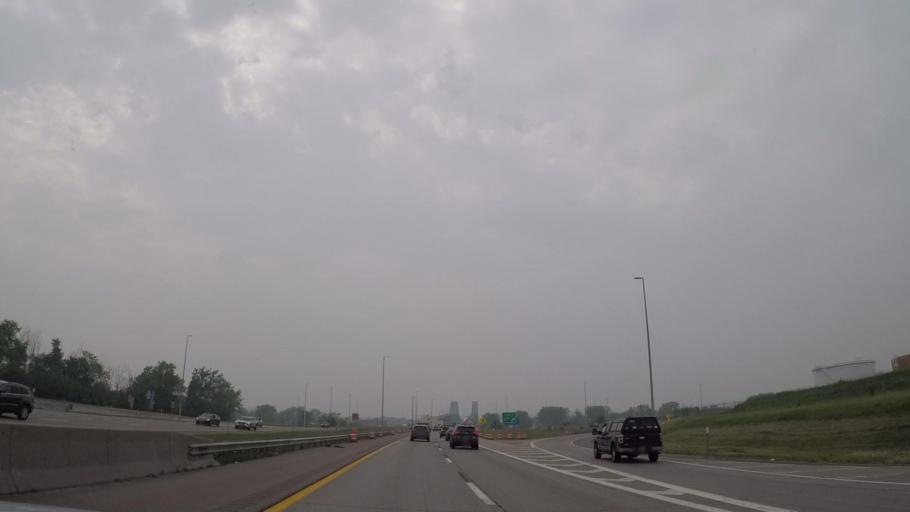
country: US
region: New York
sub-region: Erie County
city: Grandyle Village
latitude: 42.9930
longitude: -78.9266
